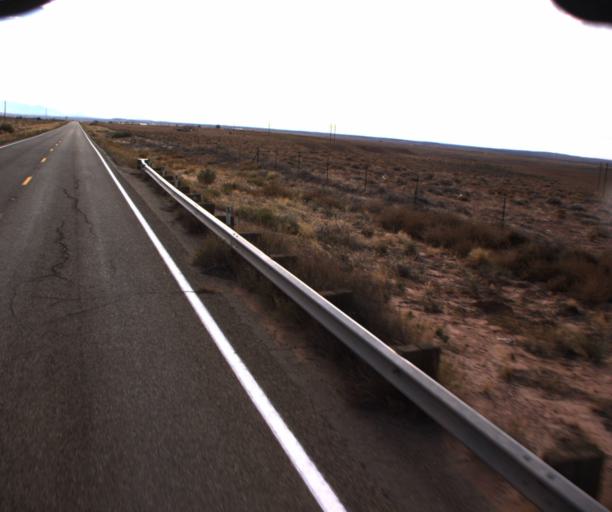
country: US
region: Arizona
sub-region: Apache County
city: Many Farms
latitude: 36.5220
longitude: -109.4933
